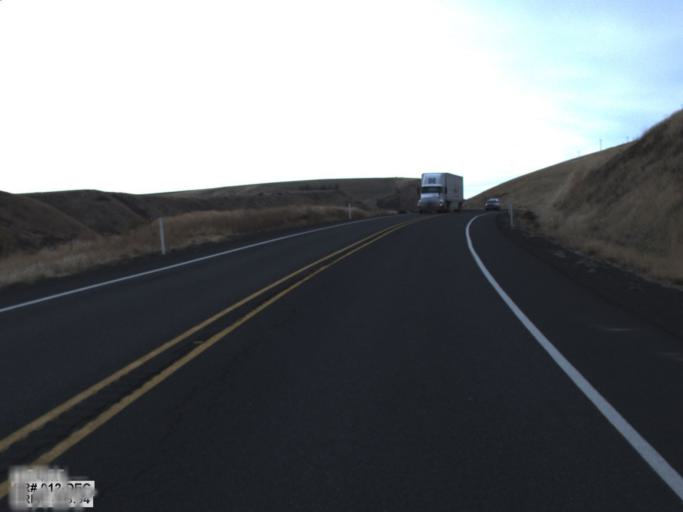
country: US
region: Washington
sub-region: Garfield County
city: Pomeroy
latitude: 46.4673
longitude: -117.4957
